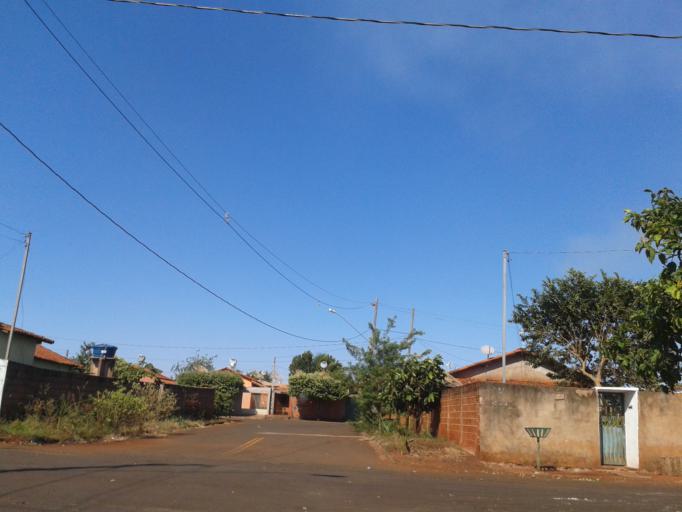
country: BR
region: Minas Gerais
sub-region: Capinopolis
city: Capinopolis
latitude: -18.5202
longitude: -49.5031
